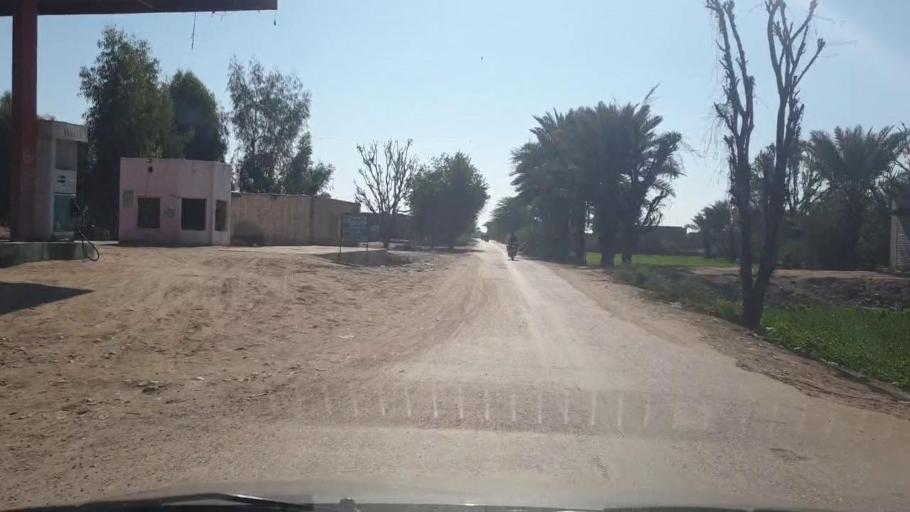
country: PK
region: Sindh
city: Bozdar
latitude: 27.1760
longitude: 68.6402
